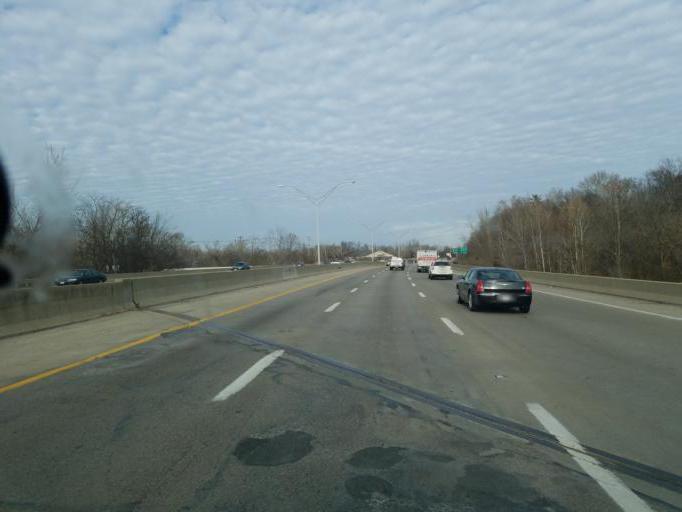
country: US
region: Ohio
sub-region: Franklin County
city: Bexley
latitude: 39.9893
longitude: -82.9378
